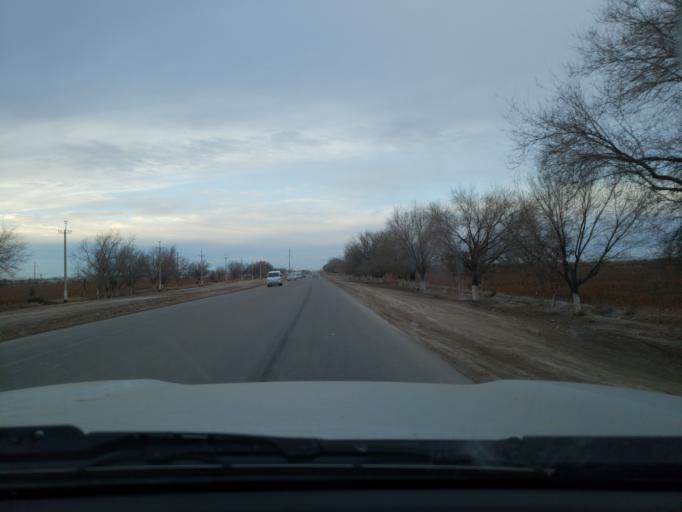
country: TM
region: Dasoguz
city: Dasoguz
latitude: 41.9197
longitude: 59.9382
